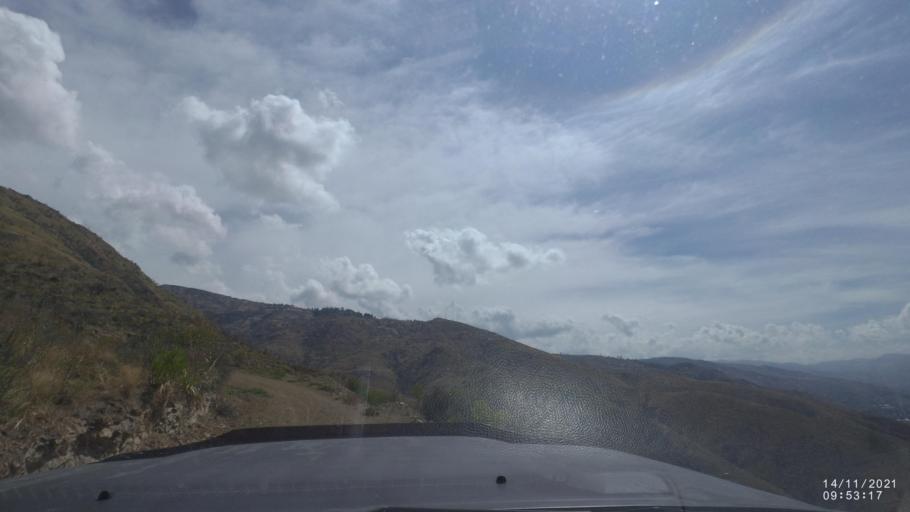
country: BO
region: Cochabamba
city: Cochabamba
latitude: -17.3600
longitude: -66.0879
